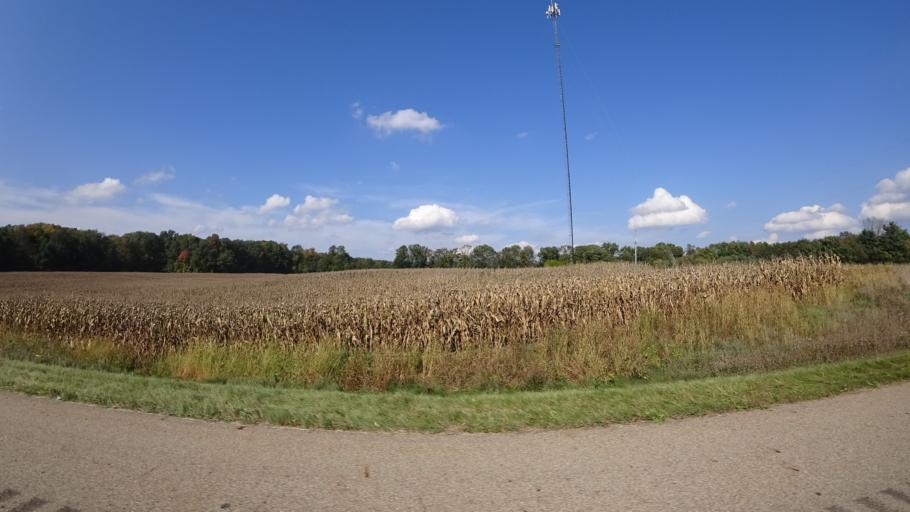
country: US
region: Michigan
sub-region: Calhoun County
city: Homer
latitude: 42.1605
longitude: -84.7654
